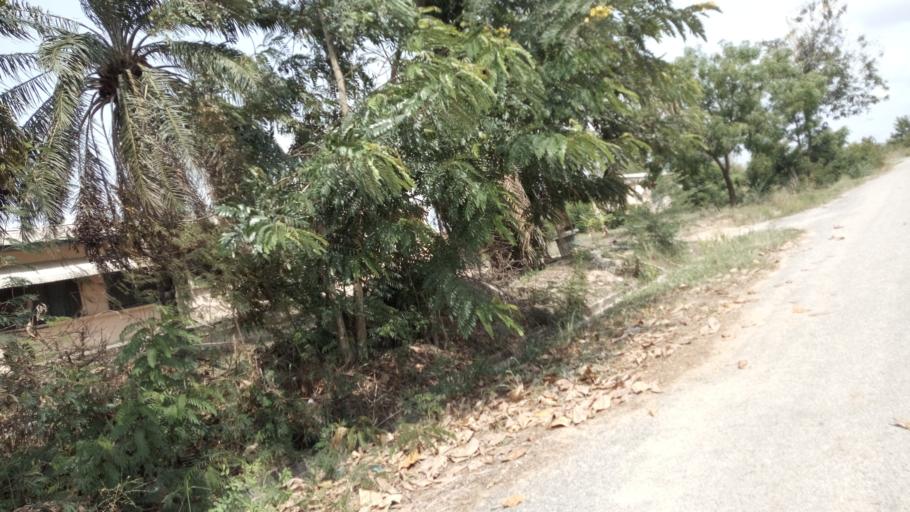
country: GH
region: Central
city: Winneba
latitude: 5.3666
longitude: -0.6447
